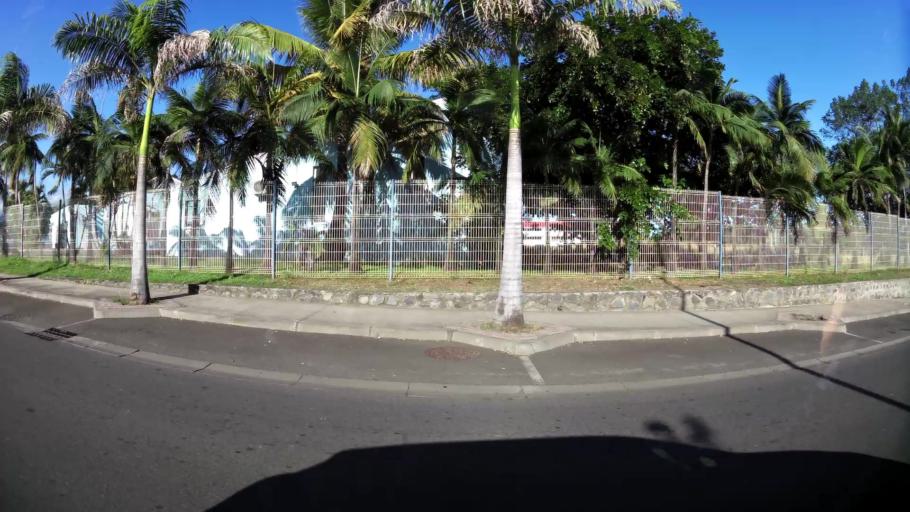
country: RE
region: Reunion
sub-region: Reunion
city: Saint-Louis
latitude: -21.2907
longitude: 55.4033
